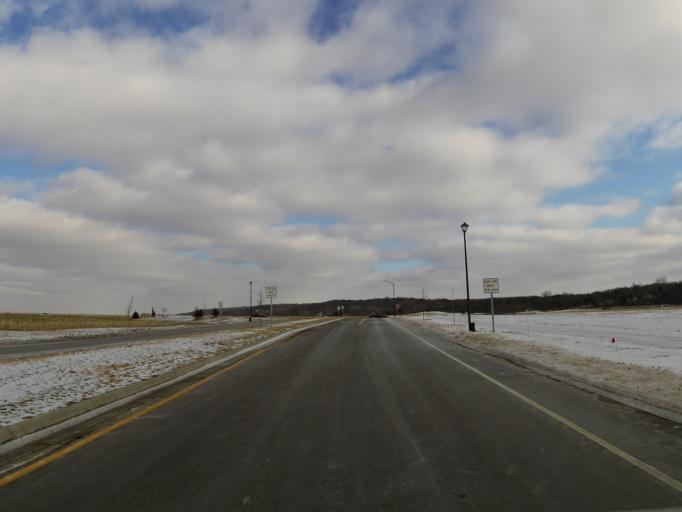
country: US
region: Minnesota
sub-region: Scott County
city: Prior Lake
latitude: 44.7624
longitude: -93.4406
